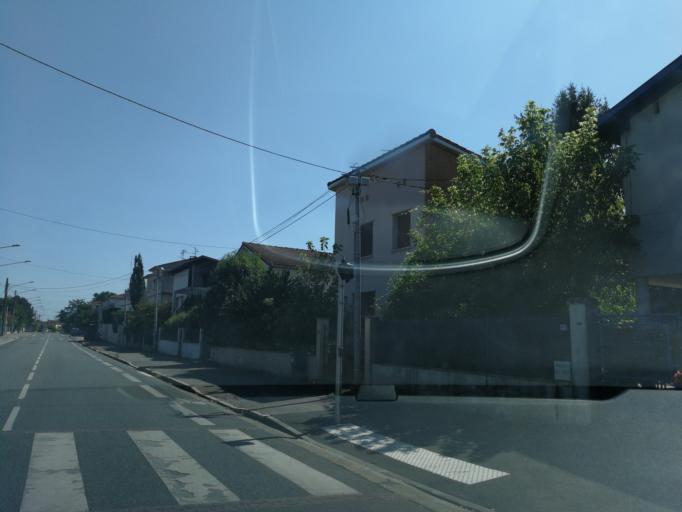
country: FR
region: Midi-Pyrenees
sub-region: Departement de la Haute-Garonne
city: Toulouse
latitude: 43.6250
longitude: 1.4654
